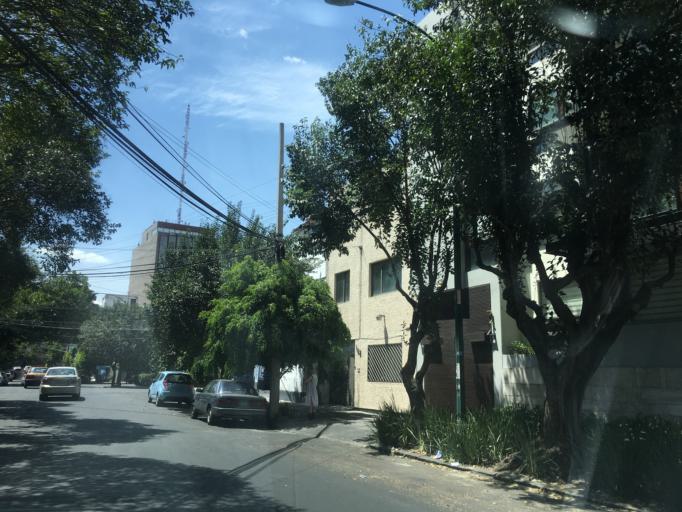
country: MX
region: Mexico City
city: Colonia del Valle
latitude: 19.3958
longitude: -99.1702
